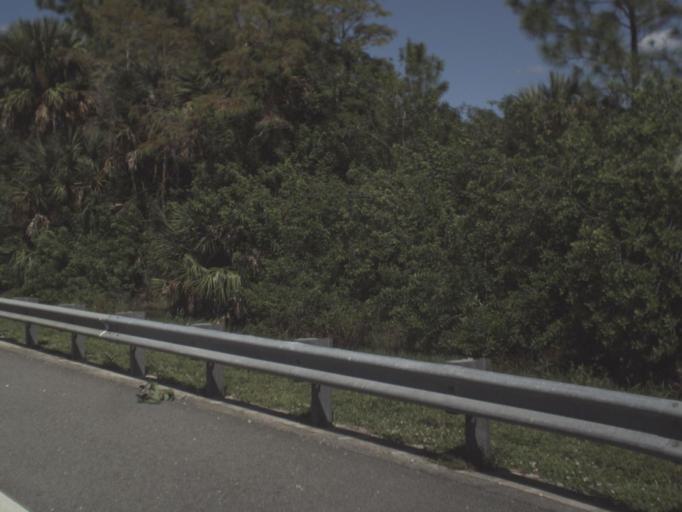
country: US
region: Florida
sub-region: Collier County
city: Lely Resort
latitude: 26.0367
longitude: -81.6575
